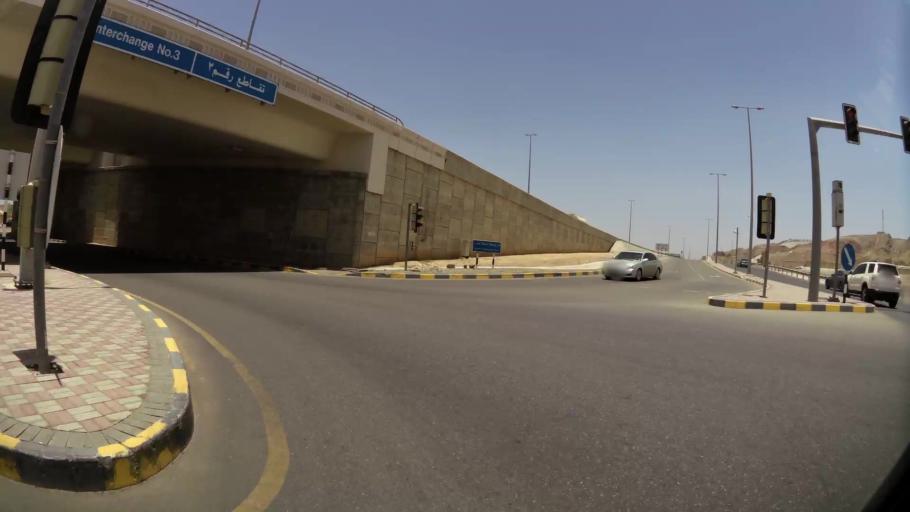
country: OM
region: Muhafazat Masqat
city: Bawshar
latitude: 23.5898
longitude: 58.4615
